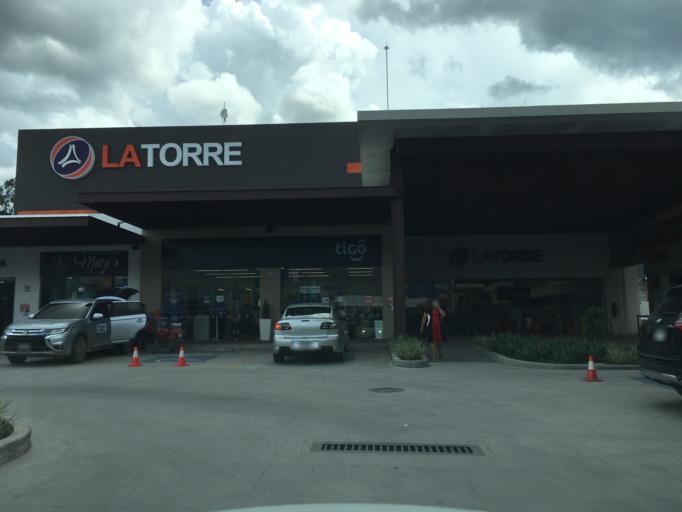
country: GT
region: Huehuetenango
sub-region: Municipio de Huehuetenango
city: Huehuetenango
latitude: 15.3079
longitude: -91.4937
